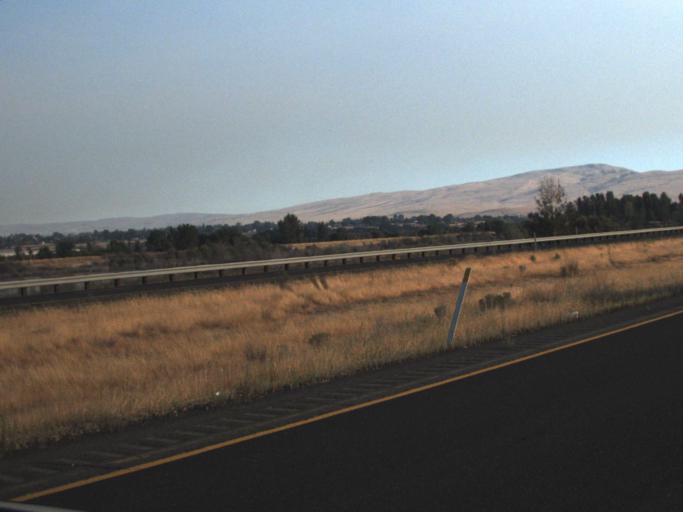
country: US
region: Washington
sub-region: Yakima County
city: Selah
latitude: 46.6613
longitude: -120.4947
